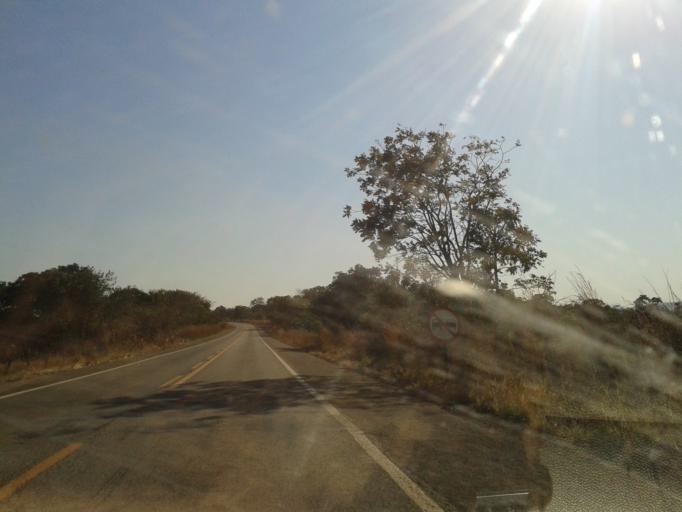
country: BR
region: Goias
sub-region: Mozarlandia
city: Mozarlandia
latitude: -14.9117
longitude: -50.5499
